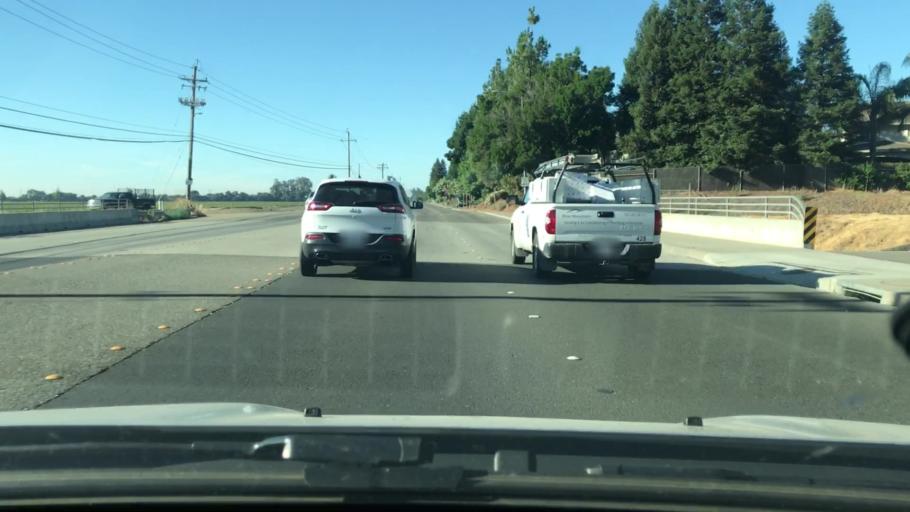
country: US
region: California
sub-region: Solano County
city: Hartley
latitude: 38.3660
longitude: -121.9340
